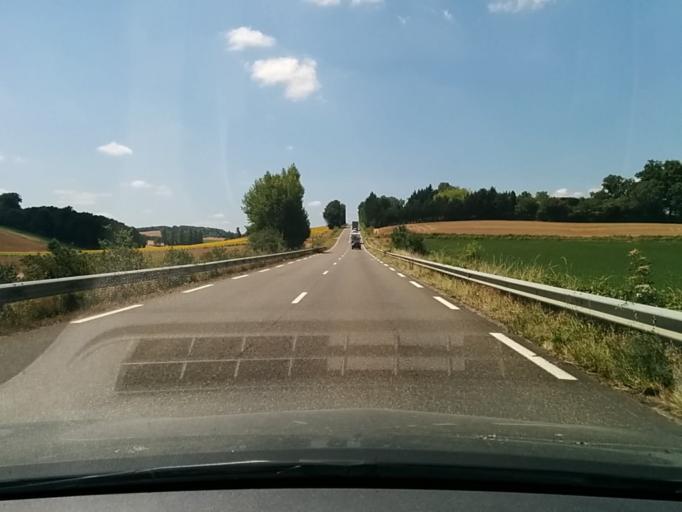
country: FR
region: Midi-Pyrenees
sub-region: Departement du Gers
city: Vic-Fezensac
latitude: 43.7575
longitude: 0.2263
